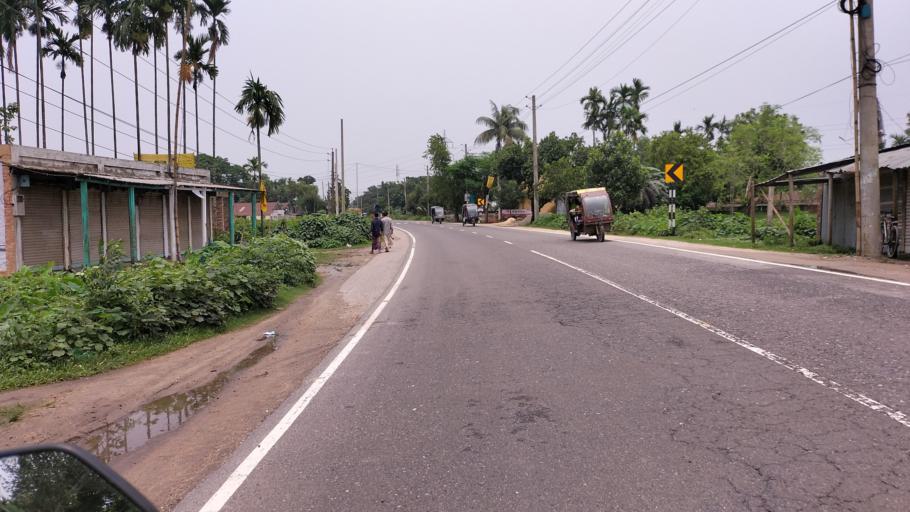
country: BD
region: Dhaka
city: Mymensingh
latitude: 24.7737
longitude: 90.4631
